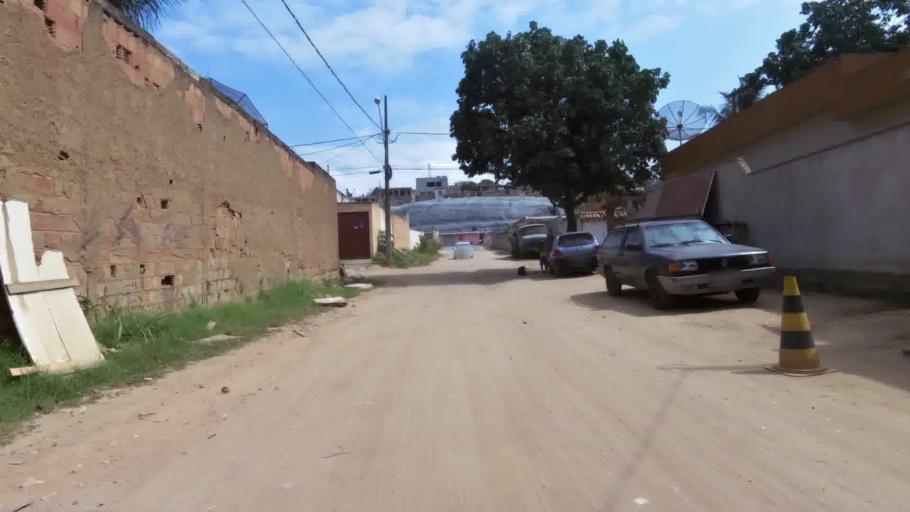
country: BR
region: Espirito Santo
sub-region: Itapemirim
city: Itapemirim
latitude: -21.0231
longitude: -40.8185
